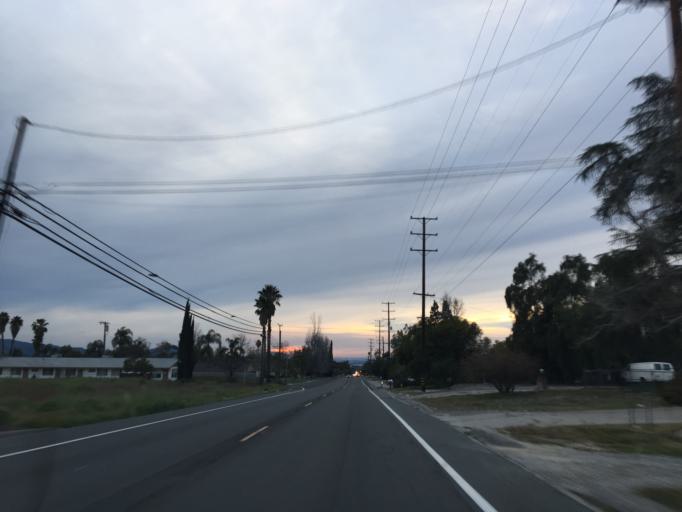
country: US
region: California
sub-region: San Bernardino County
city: Mentone
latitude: 34.0696
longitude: -117.1070
